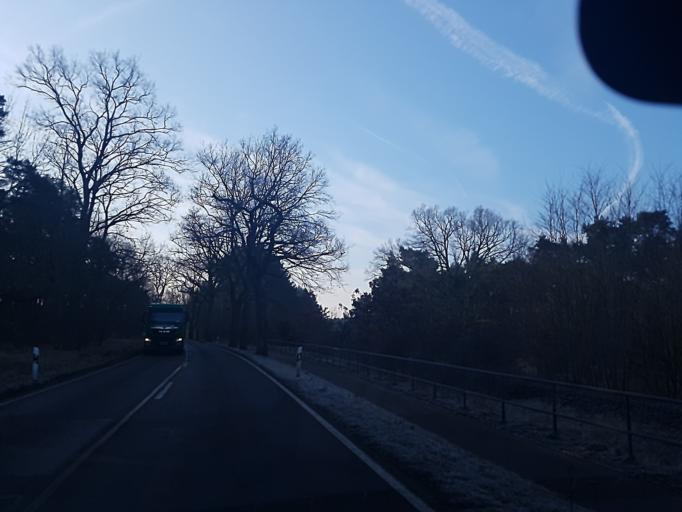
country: DE
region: Brandenburg
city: Golzow
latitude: 52.2632
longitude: 12.5989
